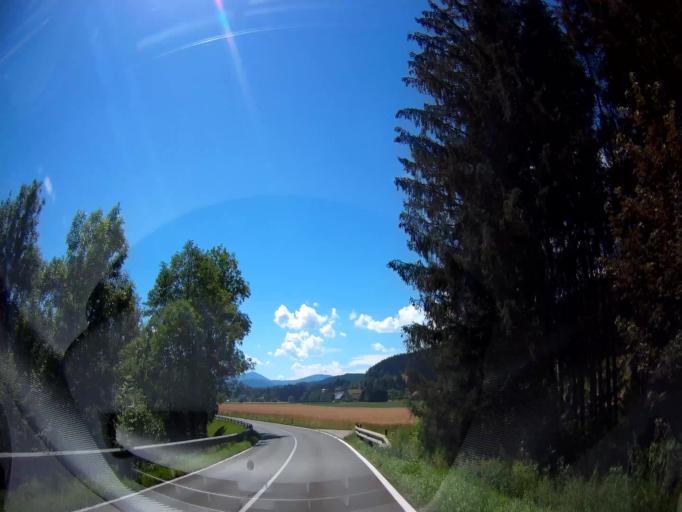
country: AT
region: Carinthia
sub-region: Politischer Bezirk Sankt Veit an der Glan
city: Glodnitz
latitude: 46.8527
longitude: 14.1829
